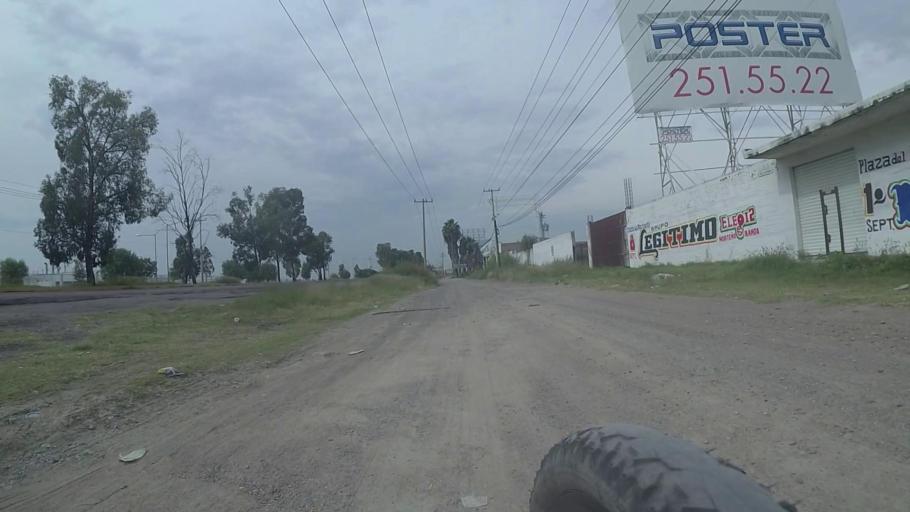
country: MX
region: Aguascalientes
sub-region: Aguascalientes
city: Penuelas (El Cienegal)
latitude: 21.7344
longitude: -102.2766
